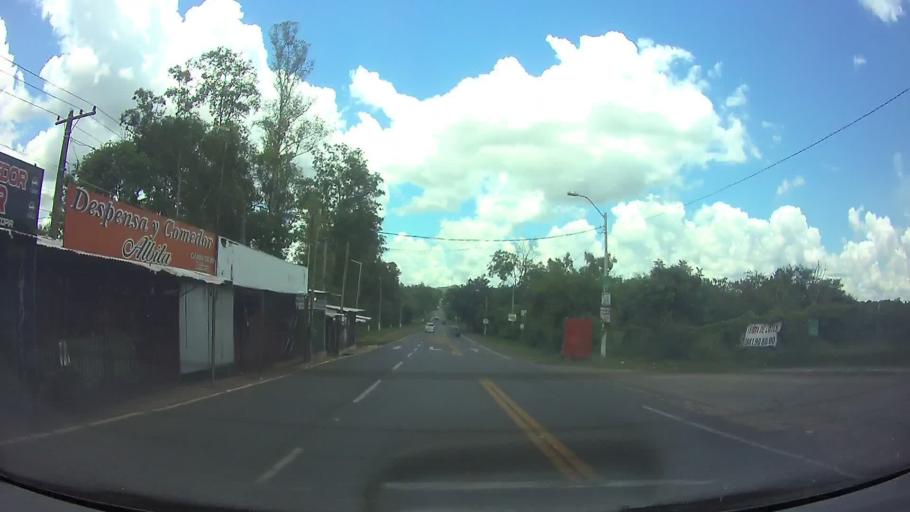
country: PY
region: Central
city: Capiata
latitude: -25.3498
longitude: -57.4177
